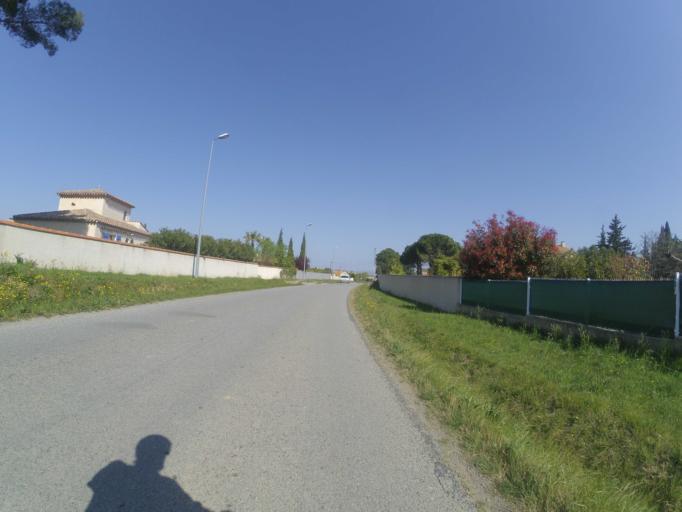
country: FR
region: Languedoc-Roussillon
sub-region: Departement des Pyrenees-Orientales
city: Llupia
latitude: 42.6149
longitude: 2.7691
